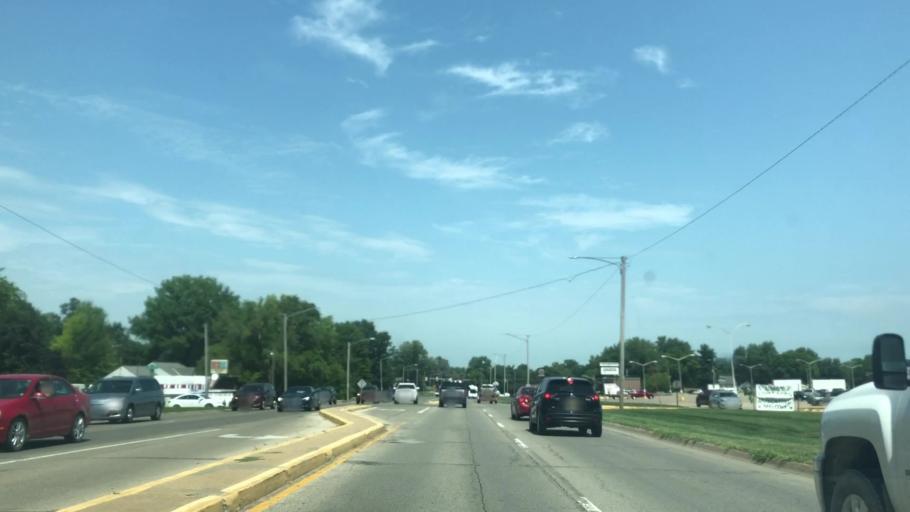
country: US
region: Iowa
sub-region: Marshall County
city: Marshalltown
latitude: 42.0256
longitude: -92.9125
